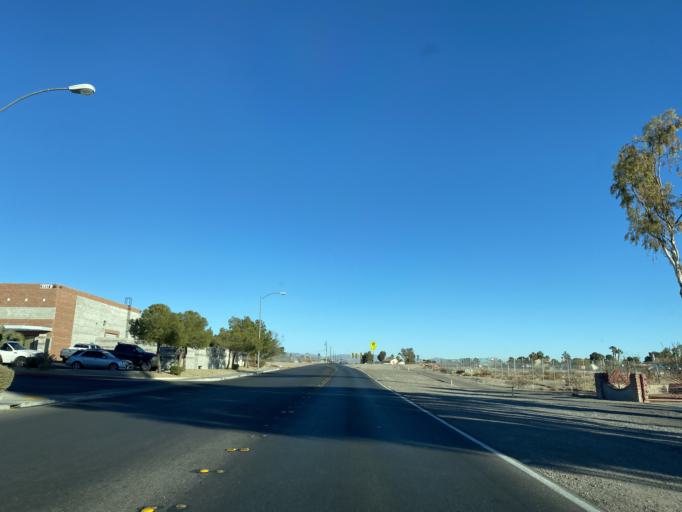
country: US
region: Nevada
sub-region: Clark County
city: Whitney
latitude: 36.0809
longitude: -115.1099
